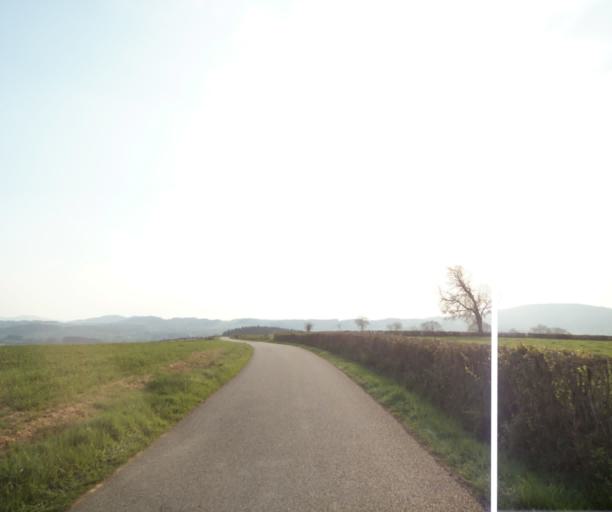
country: FR
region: Bourgogne
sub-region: Departement de Saone-et-Loire
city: Matour
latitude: 46.4141
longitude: 4.4556
